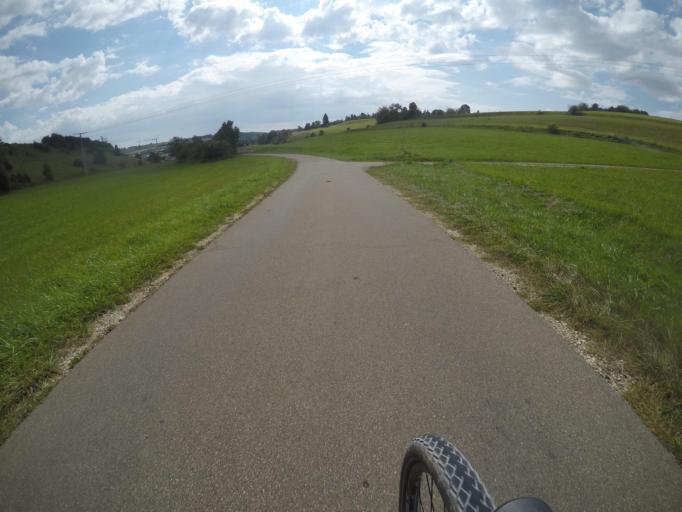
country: DE
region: Baden-Wuerttemberg
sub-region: Tuebingen Region
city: Munsingen
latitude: 48.4230
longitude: 9.4958
